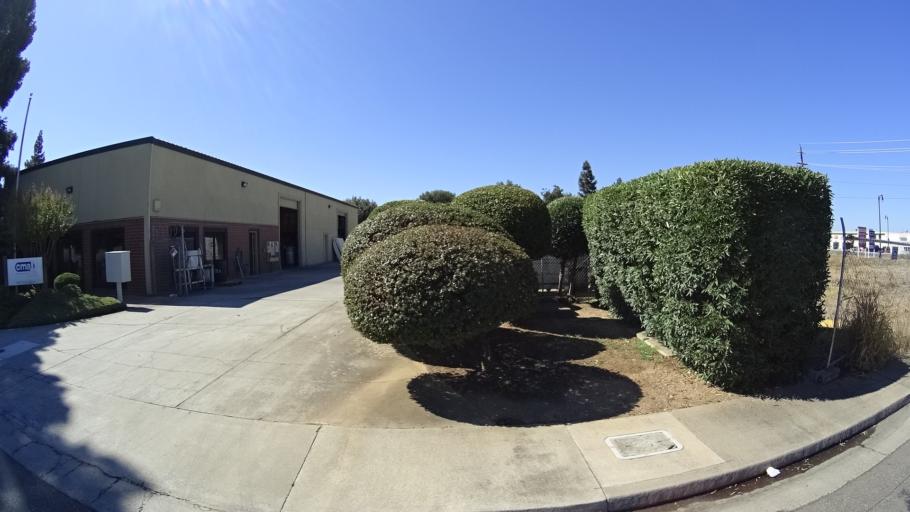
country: US
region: California
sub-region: Sacramento County
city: Elk Grove
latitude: 38.3781
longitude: -121.3580
